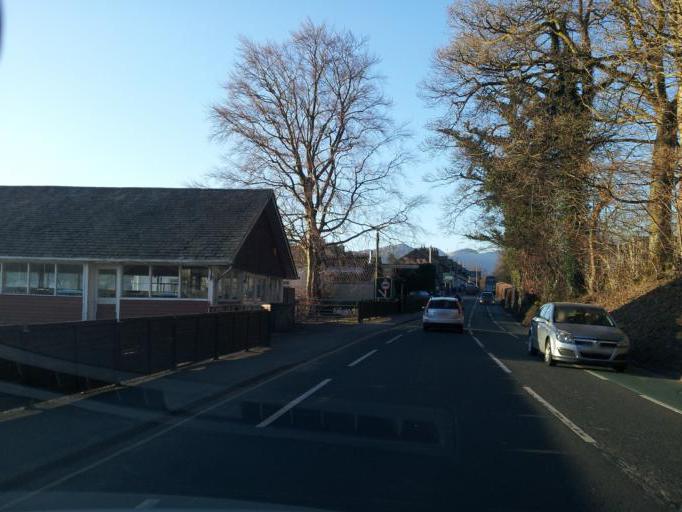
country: GB
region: England
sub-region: Cumbria
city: Ambleside
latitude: 54.4179
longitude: -2.9606
